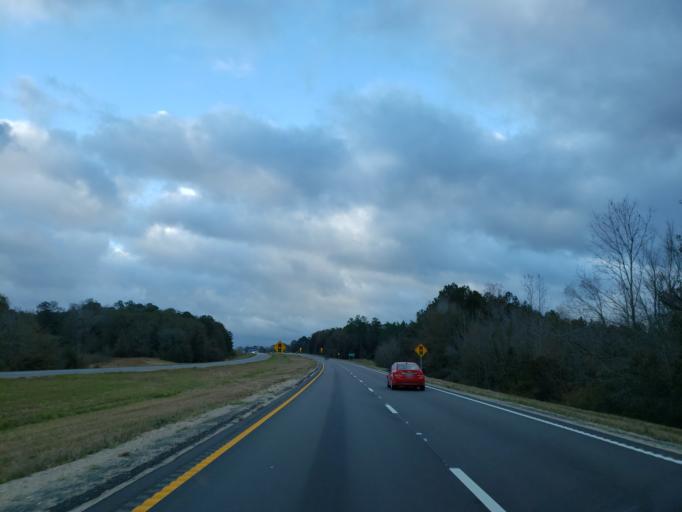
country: US
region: Mississippi
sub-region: George County
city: Lucedale
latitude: 30.9297
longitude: -88.5195
